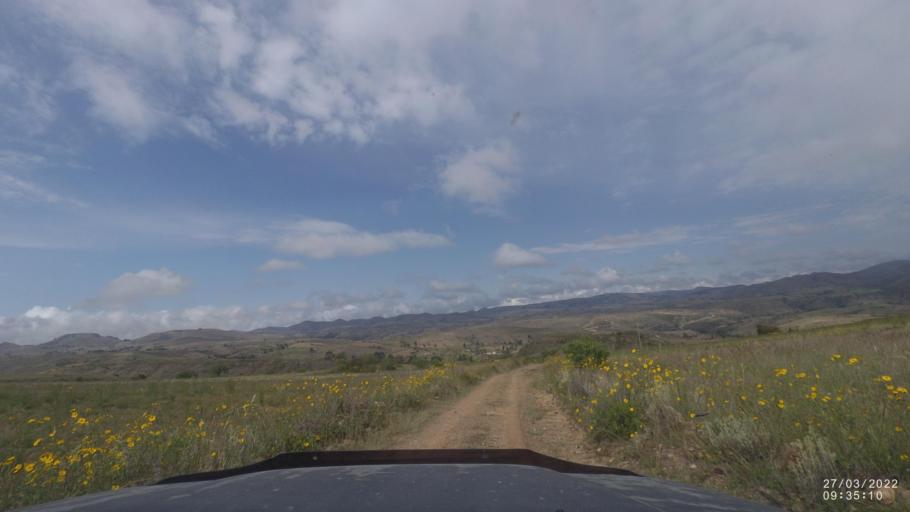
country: BO
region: Cochabamba
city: Cliza
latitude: -17.7453
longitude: -65.8920
